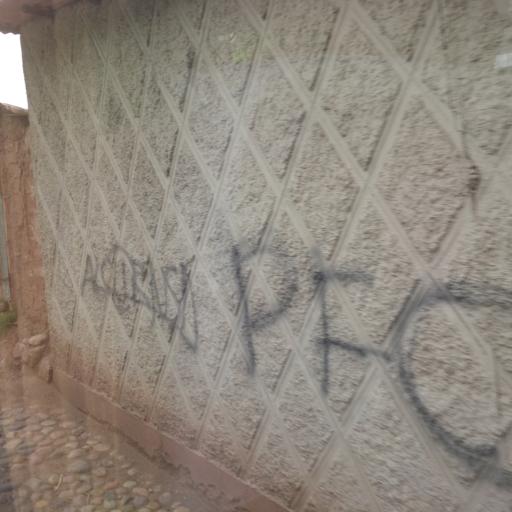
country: PE
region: Cusco
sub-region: Provincia de Cusco
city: Cusco
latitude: -13.5136
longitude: -71.9806
